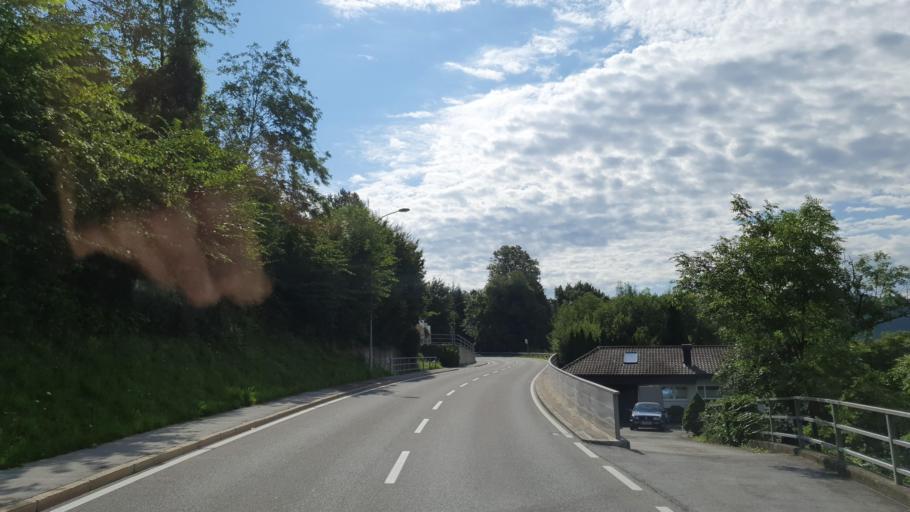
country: AT
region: Vorarlberg
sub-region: Politischer Bezirk Bregenz
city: Kennelbach
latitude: 47.4858
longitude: 9.7538
